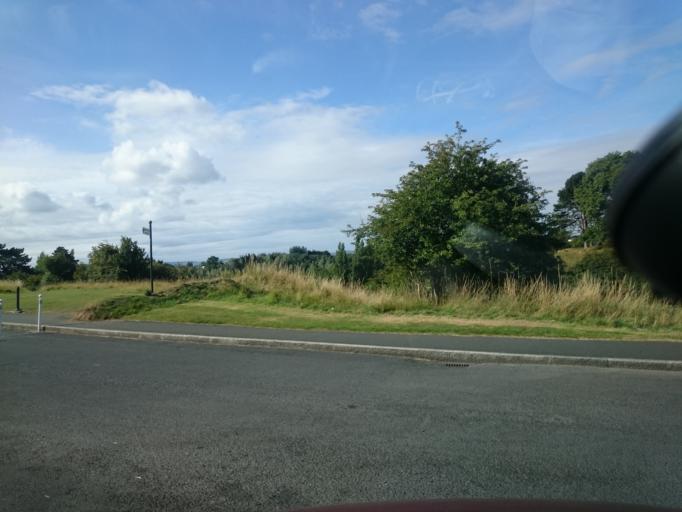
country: IE
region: Leinster
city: Chapelizod
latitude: 53.3475
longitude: -6.3271
